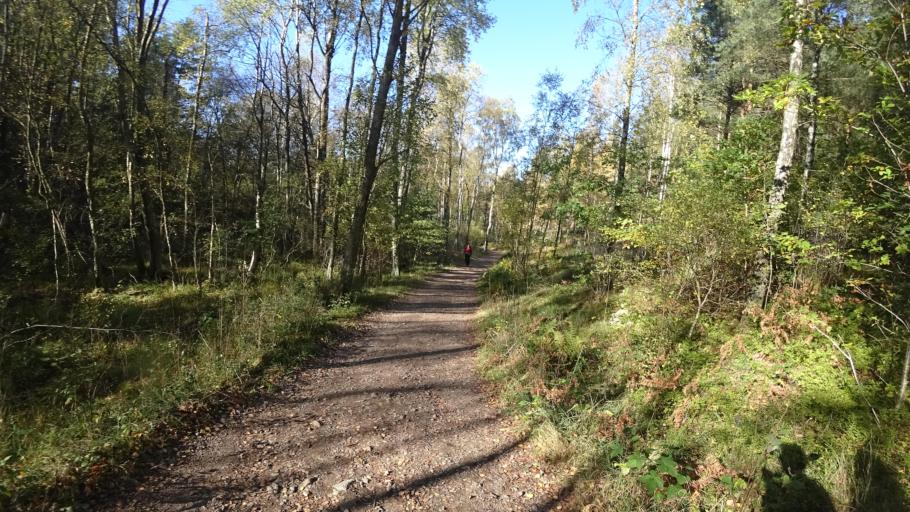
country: SE
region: Vaestra Goetaland
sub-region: Goteborg
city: Goeteborg
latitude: 57.6696
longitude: 11.9540
